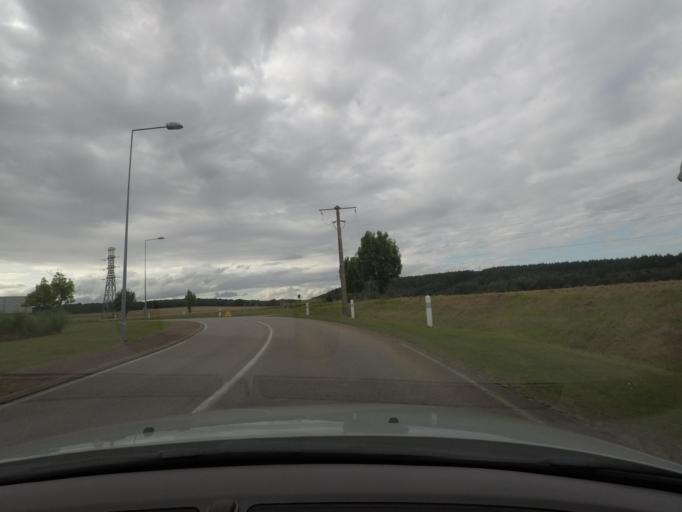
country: FR
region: Haute-Normandie
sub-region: Departement de l'Eure
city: Le Manoir
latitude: 49.3270
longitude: 1.2179
